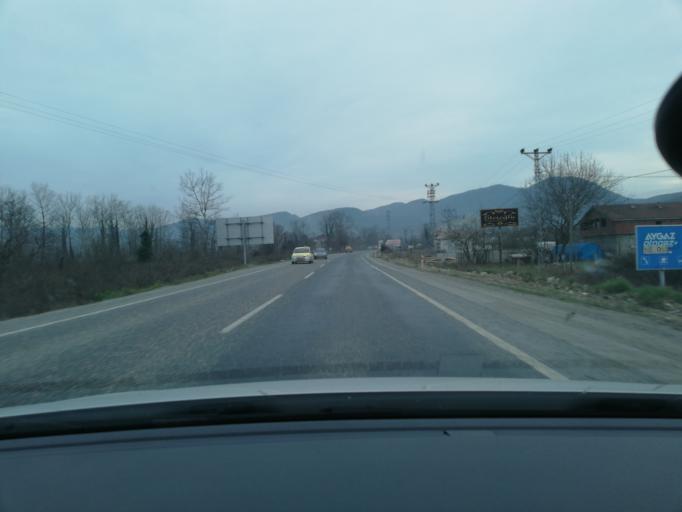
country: TR
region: Zonguldak
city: Gokcebey
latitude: 41.3014
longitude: 32.1136
